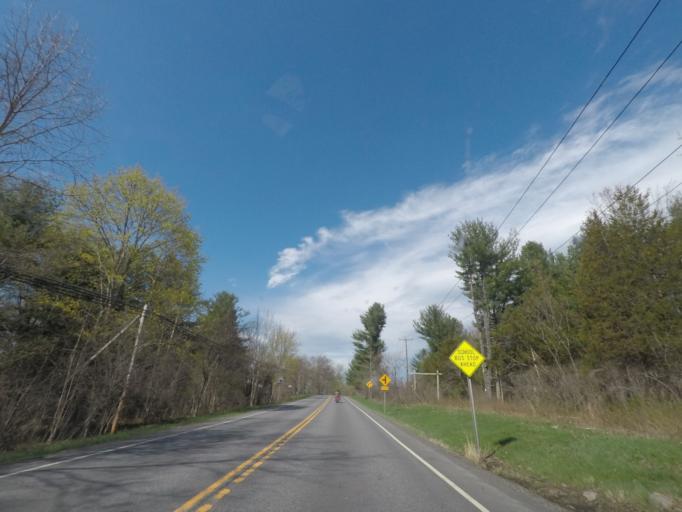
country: US
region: New York
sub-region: Greene County
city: Cairo
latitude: 42.3700
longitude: -74.0382
